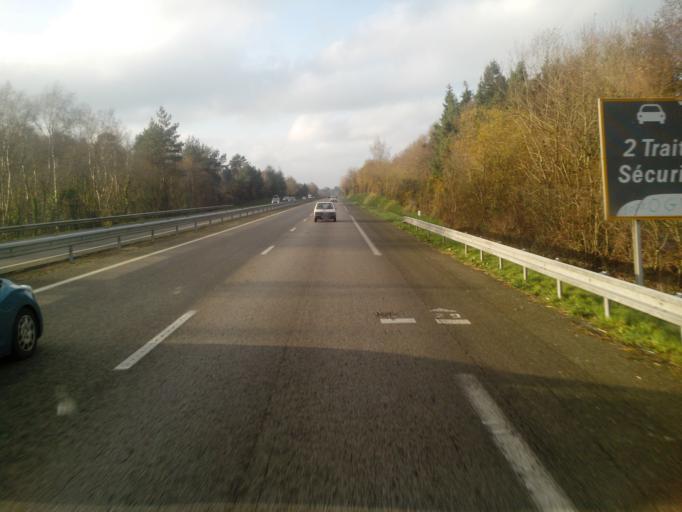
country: FR
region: Brittany
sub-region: Departement du Morbihan
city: Josselin
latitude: 47.9419
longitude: -2.5023
